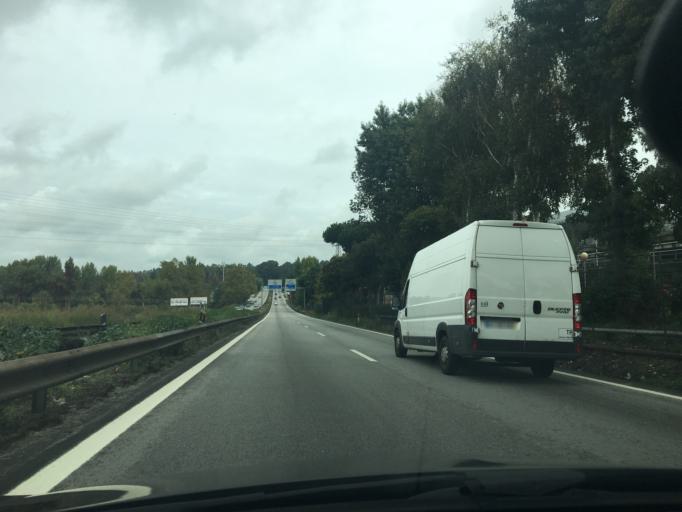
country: PT
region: Porto
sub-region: Maia
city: Leca do Bailio
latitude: 41.2145
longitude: -8.6270
